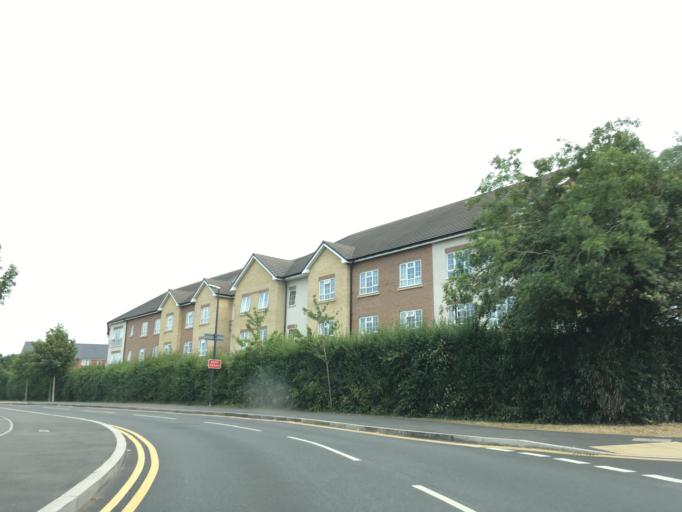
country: GB
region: England
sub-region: South Gloucestershire
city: Stoke Gifford
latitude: 51.4967
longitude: -2.5590
